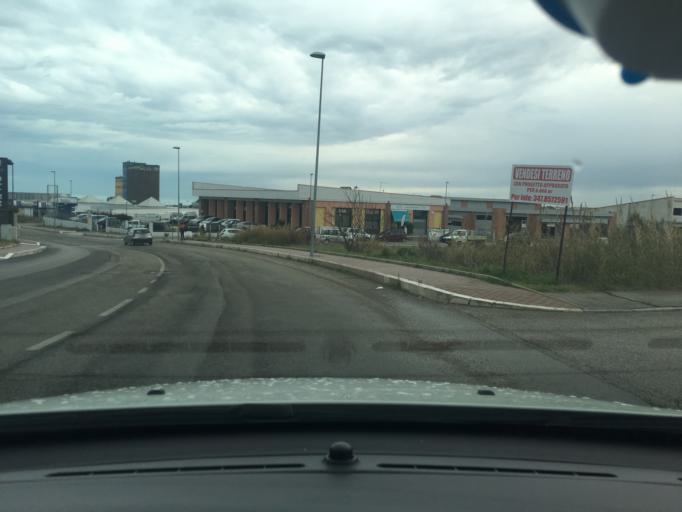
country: IT
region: Molise
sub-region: Provincia di Campobasso
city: Termoli
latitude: 41.9818
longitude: 15.0026
